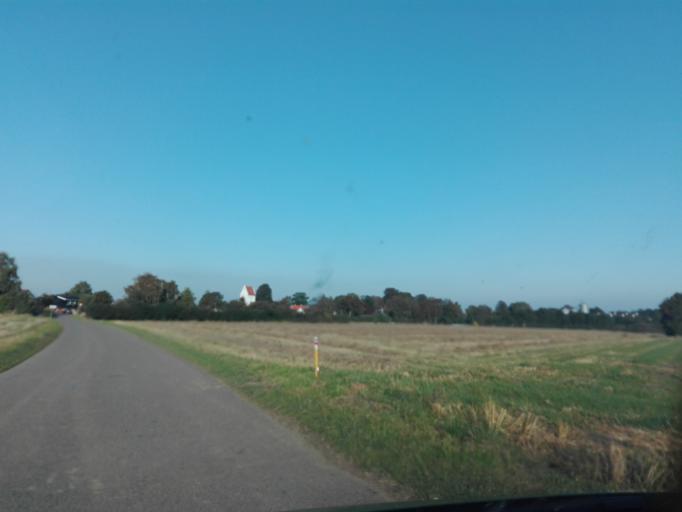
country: DK
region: Central Jutland
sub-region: Odder Kommune
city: Odder
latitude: 55.9271
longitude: 10.1874
